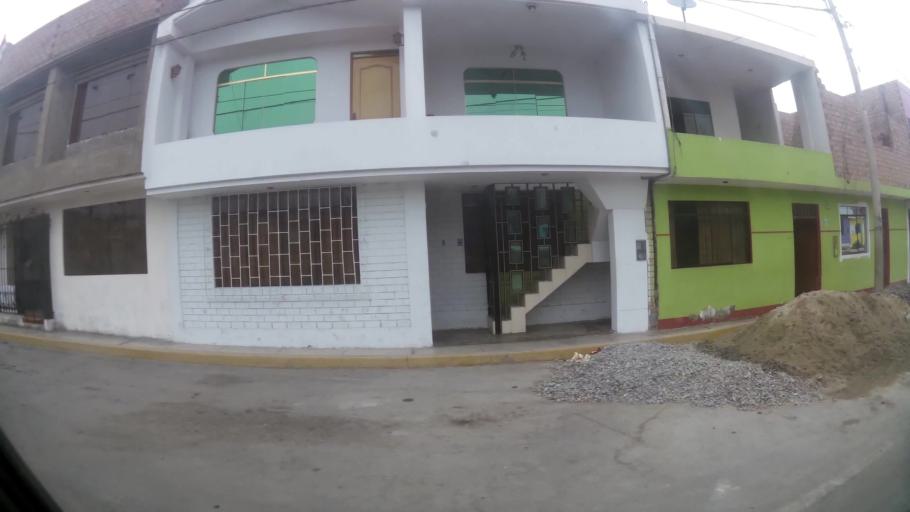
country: PE
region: Lima
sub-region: Provincia de Huaral
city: Chancay
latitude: -11.5904
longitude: -77.2599
